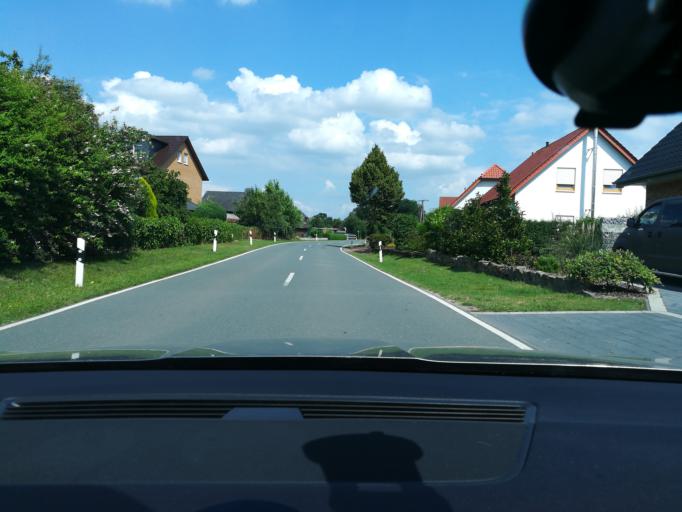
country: DE
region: North Rhine-Westphalia
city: Espelkamp
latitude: 52.3444
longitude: 8.6412
